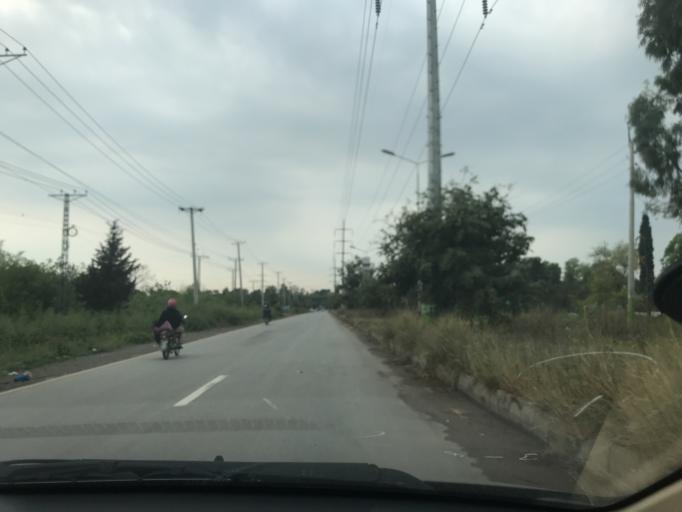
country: PK
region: Punjab
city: Rawalpindi
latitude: 33.6764
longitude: 73.1476
